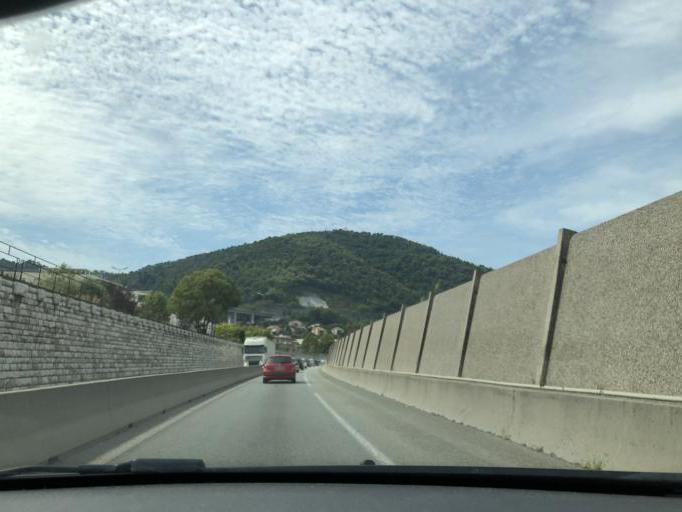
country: FR
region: Provence-Alpes-Cote d'Azur
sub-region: Departement des Alpes-Maritimes
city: La Trinite
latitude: 43.7381
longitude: 7.3090
